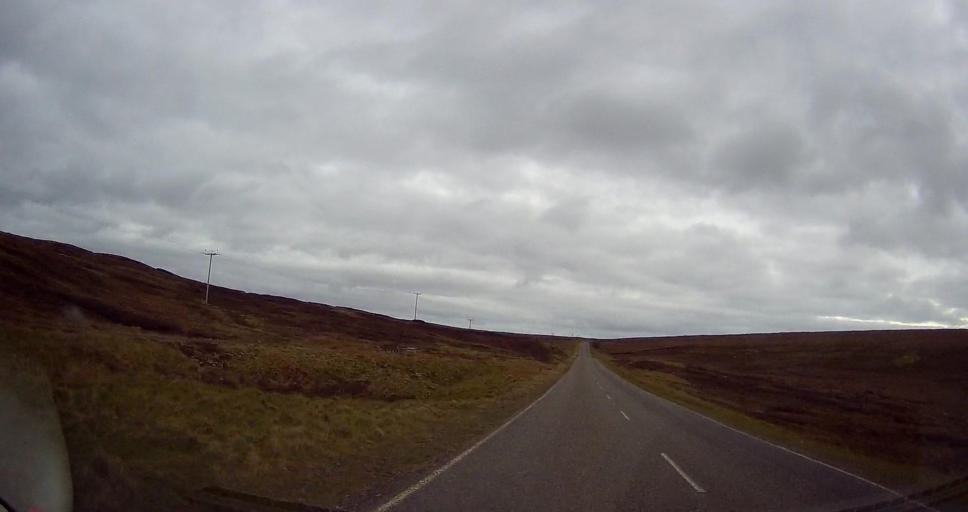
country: GB
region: Scotland
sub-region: Shetland Islands
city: Shetland
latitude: 60.6682
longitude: -1.0134
